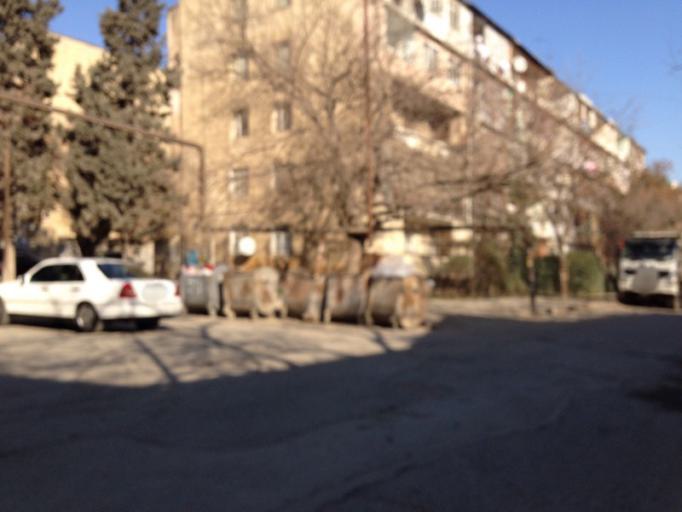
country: AZ
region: Baki
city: Baku
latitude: 40.4029
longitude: 49.8751
